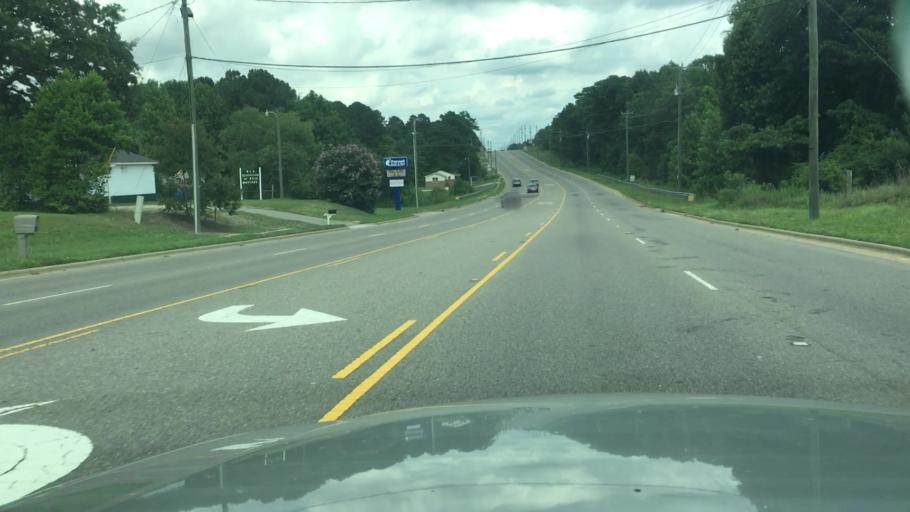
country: US
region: North Carolina
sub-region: Cumberland County
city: Hope Mills
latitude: 35.0103
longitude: -78.9519
